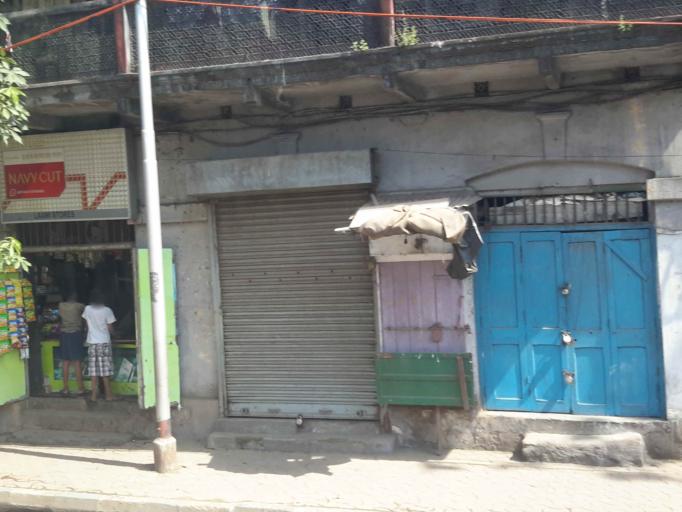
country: IN
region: West Bengal
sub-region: Kolkata
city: Kolkata
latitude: 22.5415
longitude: 88.3641
